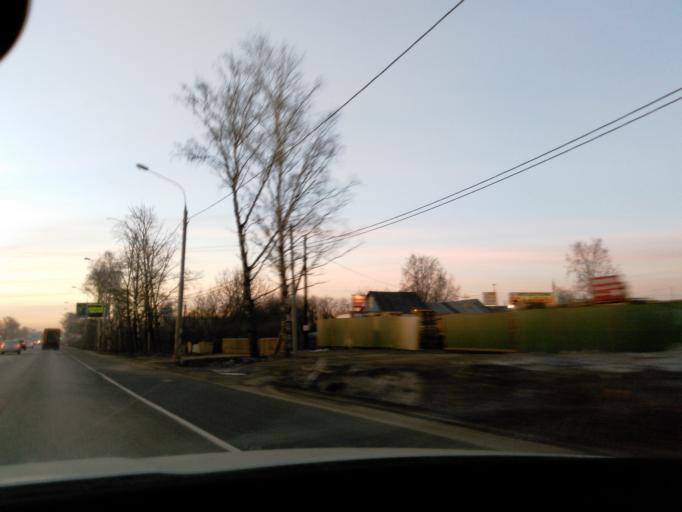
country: RU
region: Moskovskaya
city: Novopodrezkovo
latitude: 55.9628
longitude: 37.3322
